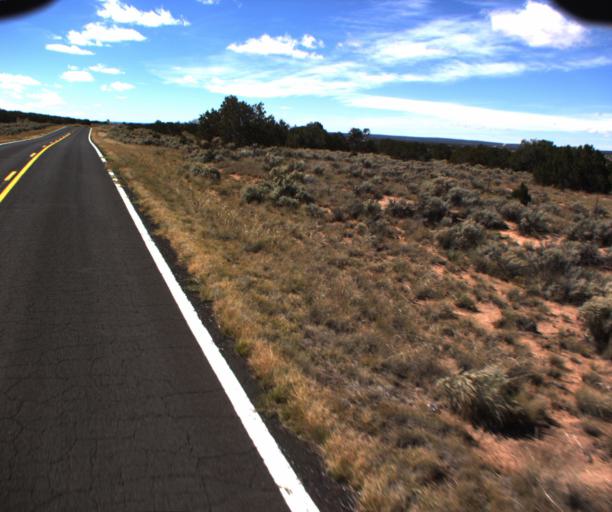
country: US
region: Arizona
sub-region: Apache County
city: Houck
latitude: 34.9098
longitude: -109.2255
